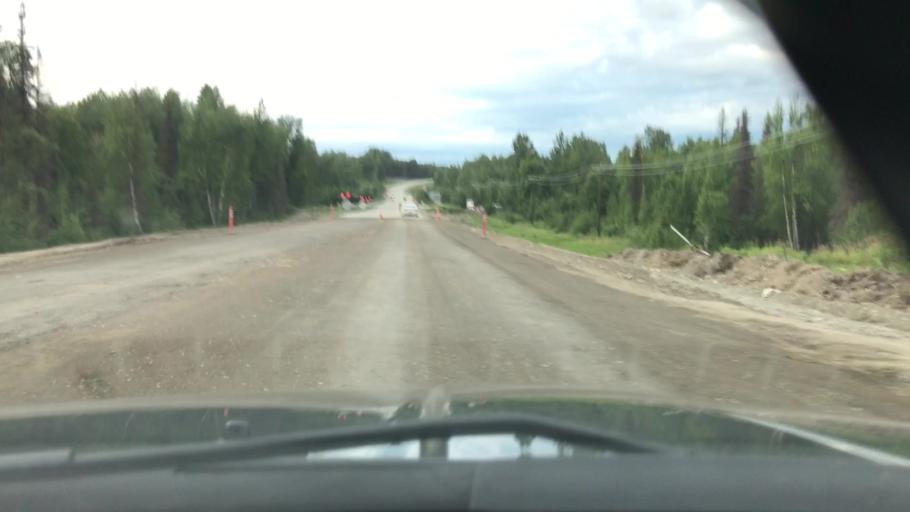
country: US
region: Alaska
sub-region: Matanuska-Susitna Borough
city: Y
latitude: 62.1006
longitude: -150.0608
